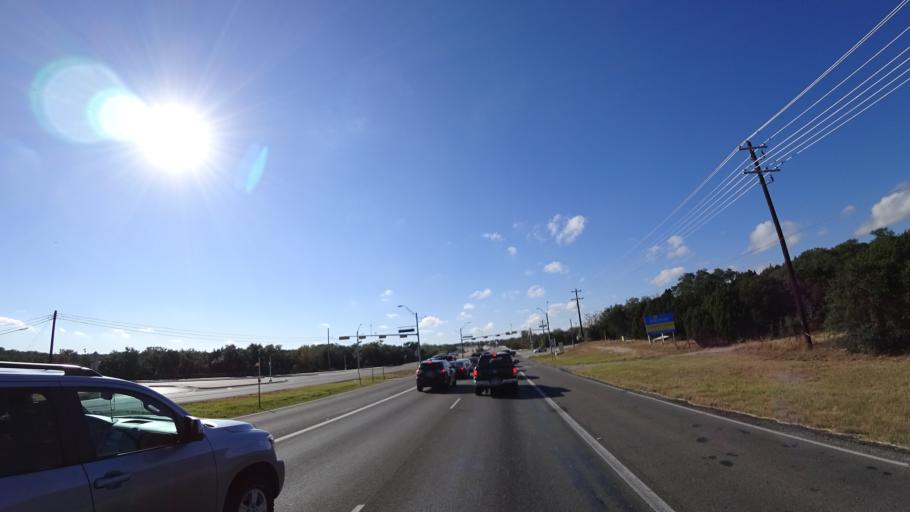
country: US
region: Texas
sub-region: Williamson County
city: Brushy Creek
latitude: 30.5086
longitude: -97.7754
